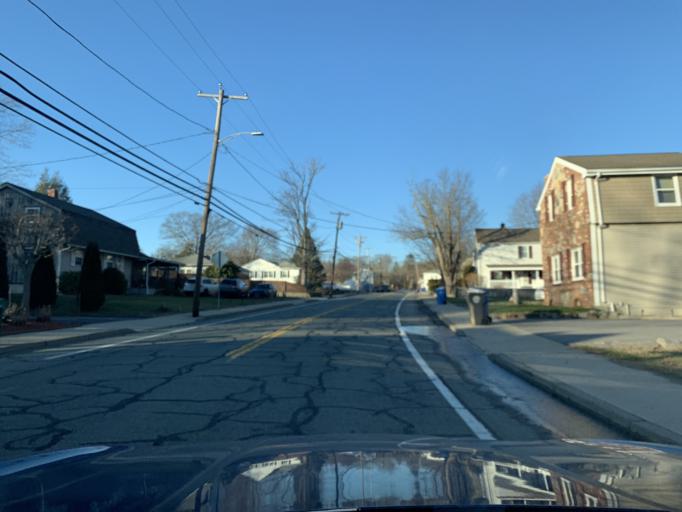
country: US
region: Rhode Island
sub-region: Kent County
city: West Warwick
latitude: 41.7319
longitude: -71.5476
